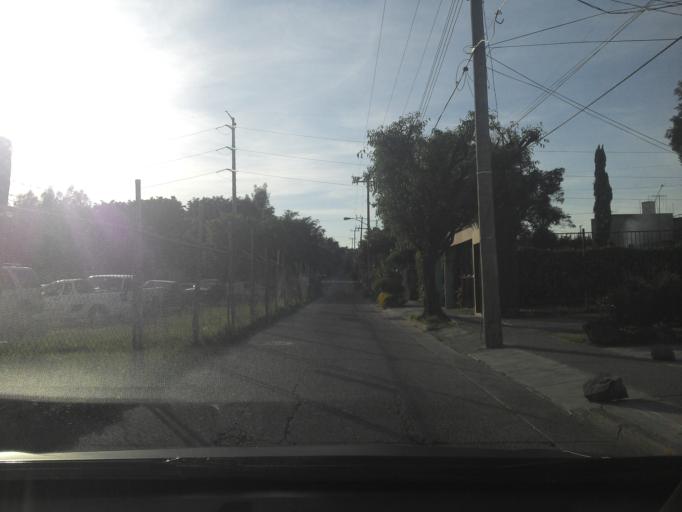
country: MX
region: Jalisco
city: Tlaquepaque
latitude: 20.6203
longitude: -103.3245
